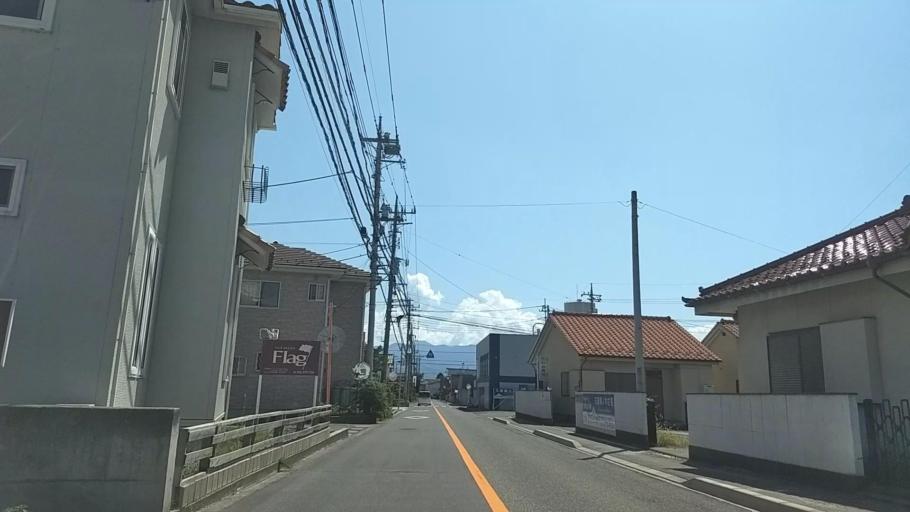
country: JP
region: Yamanashi
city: Ryuo
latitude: 35.6509
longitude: 138.5164
